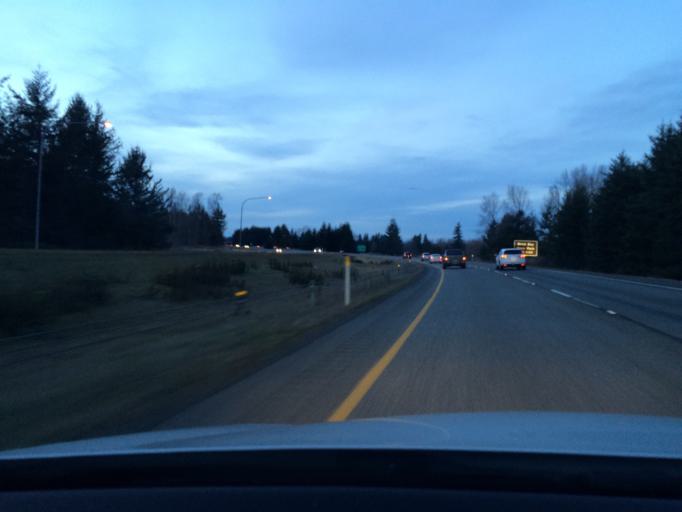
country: US
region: Washington
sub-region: Whatcom County
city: Ferndale
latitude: 48.8861
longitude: -122.5891
